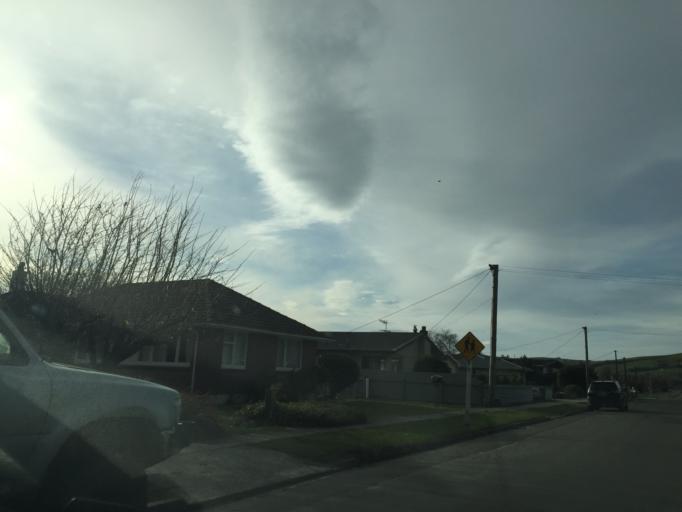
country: NZ
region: Southland
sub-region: Gore District
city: Gore
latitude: -46.1142
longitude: 168.9315
